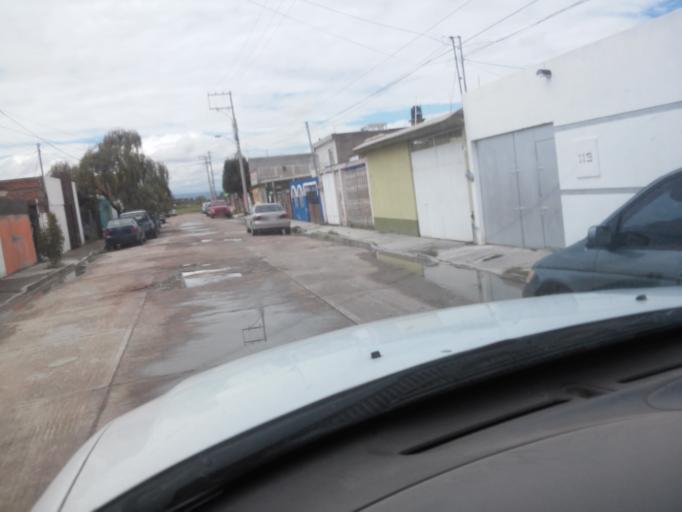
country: MX
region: Durango
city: Victoria de Durango
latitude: 24.0234
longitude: -104.6158
